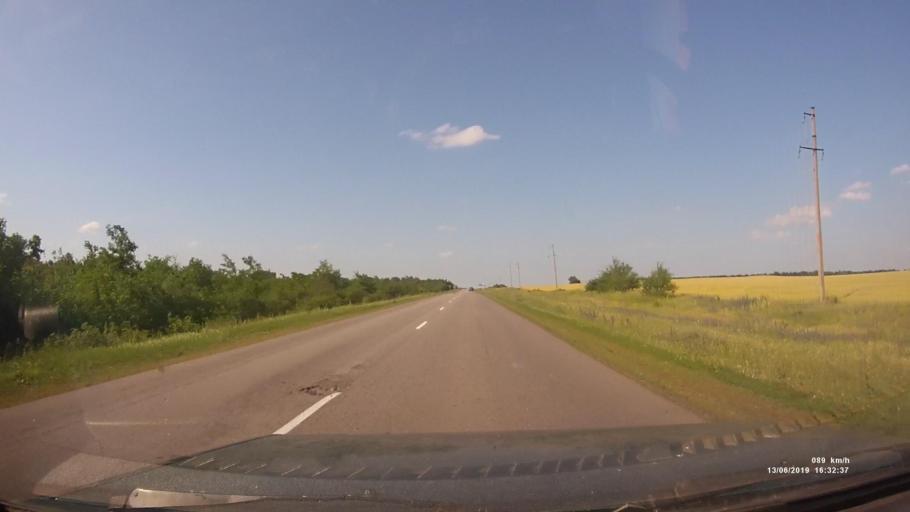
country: RU
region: Rostov
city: Kazanskaya
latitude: 49.8504
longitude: 41.2726
